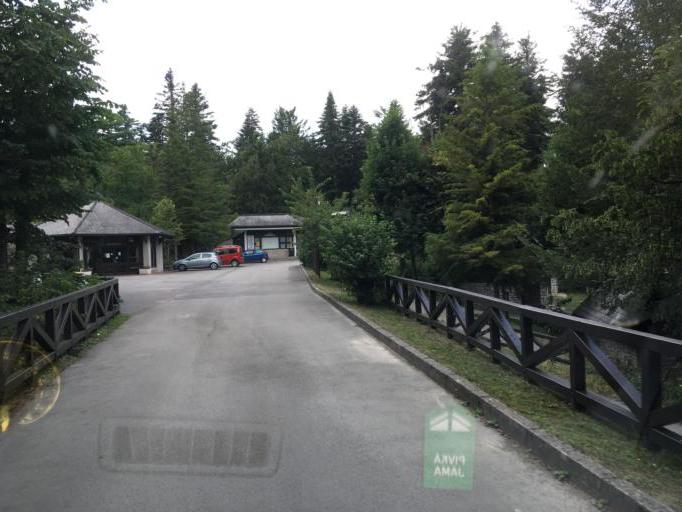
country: SI
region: Postojna
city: Postojna
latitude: 45.8048
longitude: 14.2049
